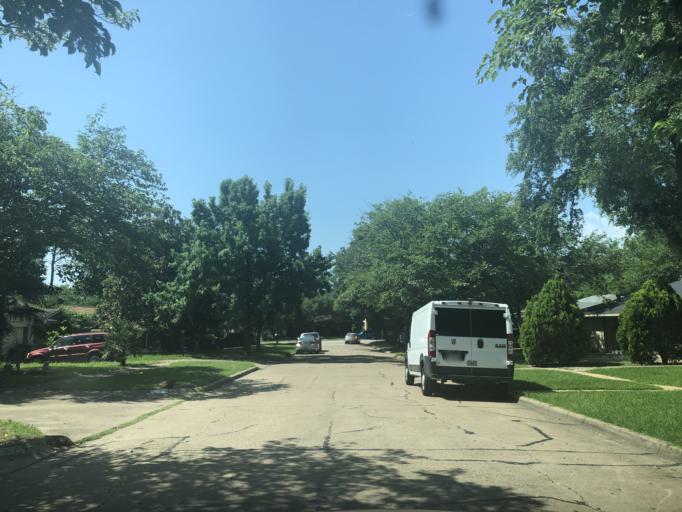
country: US
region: Texas
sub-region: Dallas County
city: Grand Prairie
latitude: 32.7328
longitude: -97.0027
